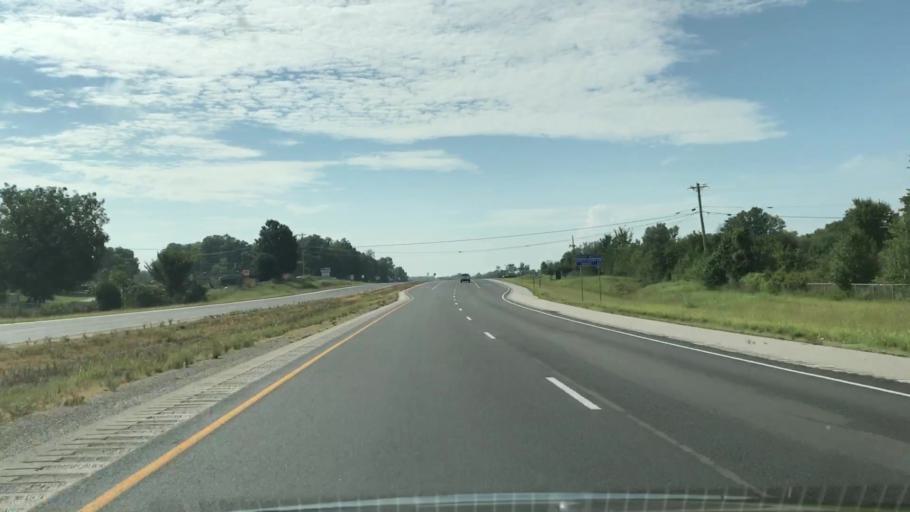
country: US
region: Kentucky
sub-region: Warren County
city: Plano
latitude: 36.8757
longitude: -86.3554
